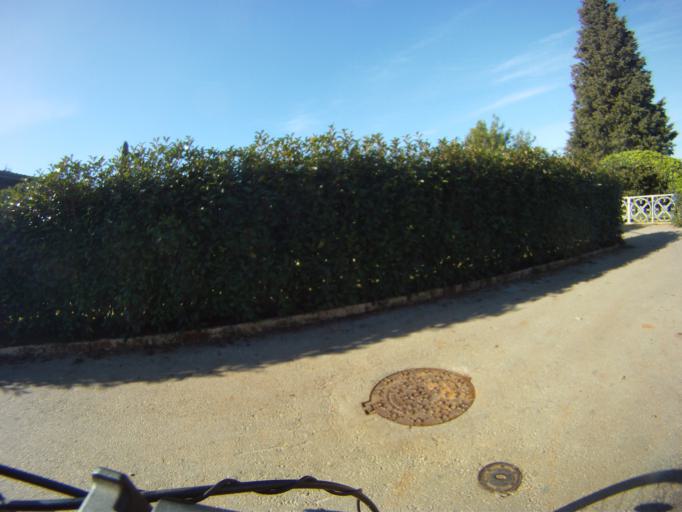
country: HR
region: Istarska
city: Novigrad
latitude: 45.3533
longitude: 13.5489
